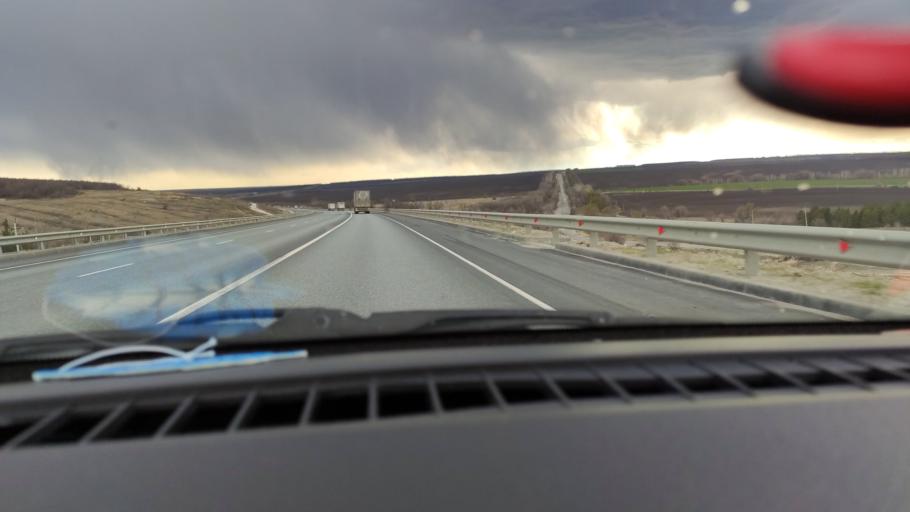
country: RU
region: Saratov
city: Yelshanka
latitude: 51.8768
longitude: 46.5070
